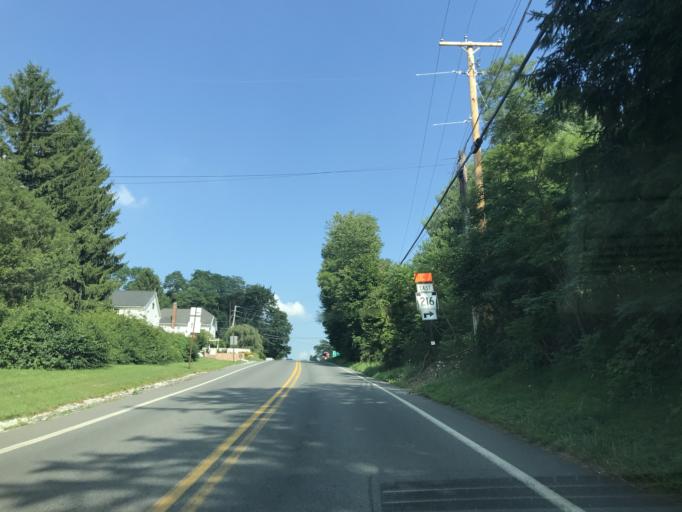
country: US
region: Pennsylvania
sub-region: York County
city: Glen Rock
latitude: 39.7495
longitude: -76.8064
